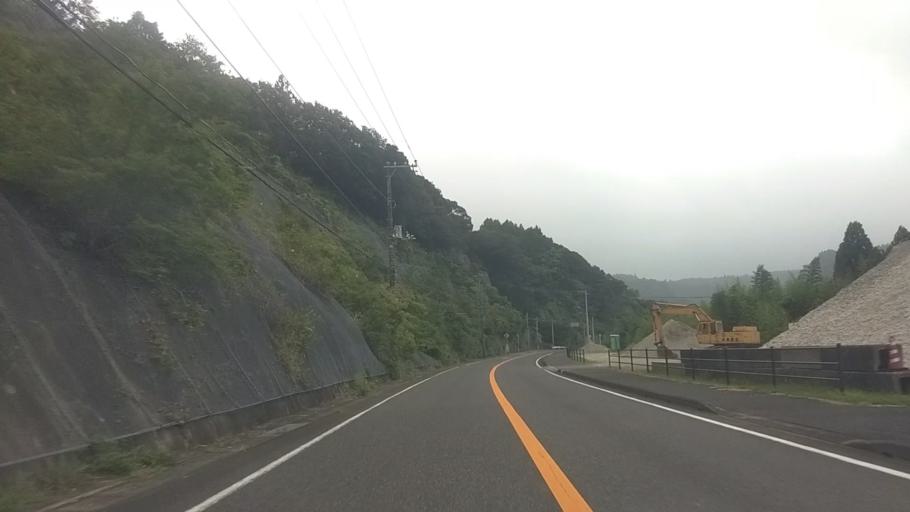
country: JP
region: Chiba
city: Katsuura
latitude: 35.2452
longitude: 140.2365
